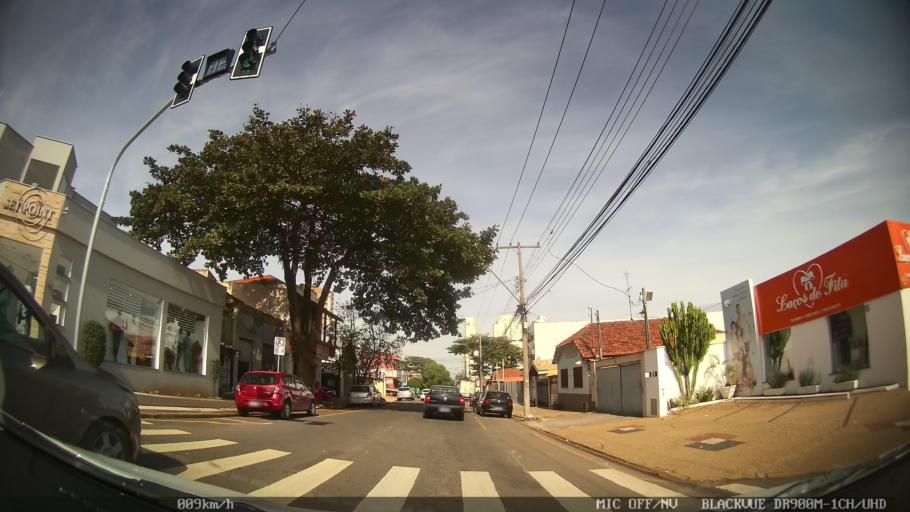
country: BR
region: Sao Paulo
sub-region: Piracicaba
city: Piracicaba
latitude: -22.7134
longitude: -47.6569
